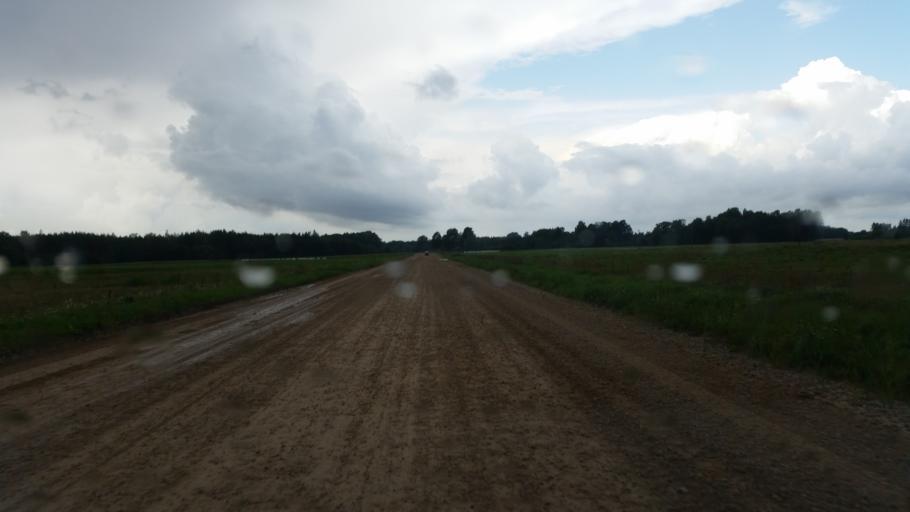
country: LV
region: Vecumnieki
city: Vecumnieki
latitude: 56.4290
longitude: 24.4596
